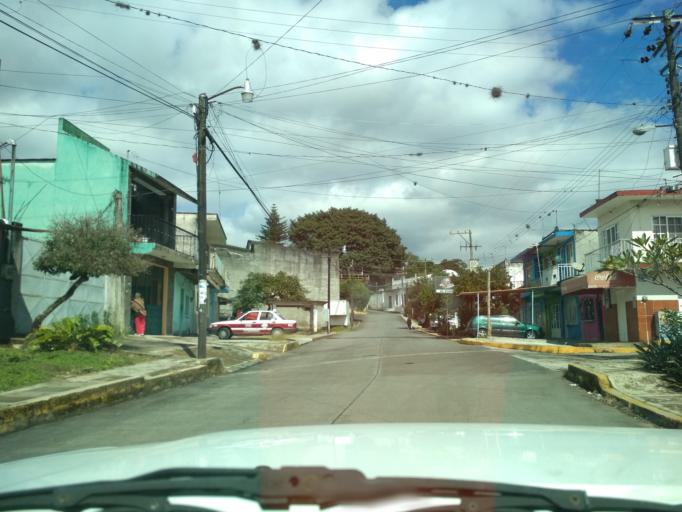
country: MX
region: Veracruz
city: Coatepec
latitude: 19.4509
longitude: -96.9368
